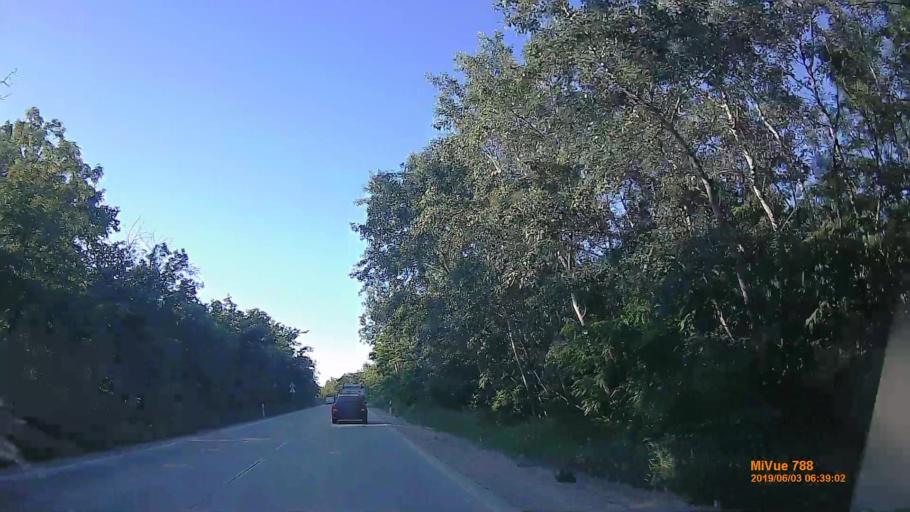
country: HU
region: Pest
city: Dunavarsany
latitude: 47.2904
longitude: 19.0966
